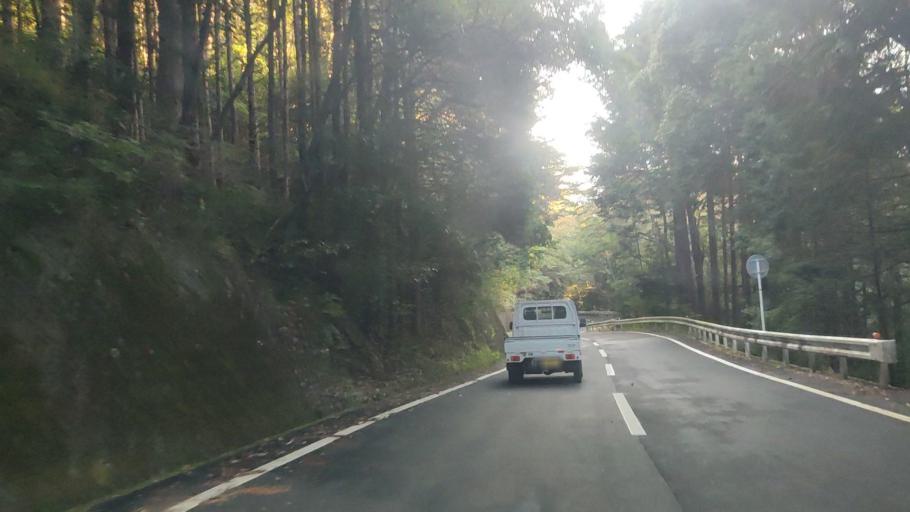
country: JP
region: Shizuoka
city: Mishima
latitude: 35.1329
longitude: 138.9771
